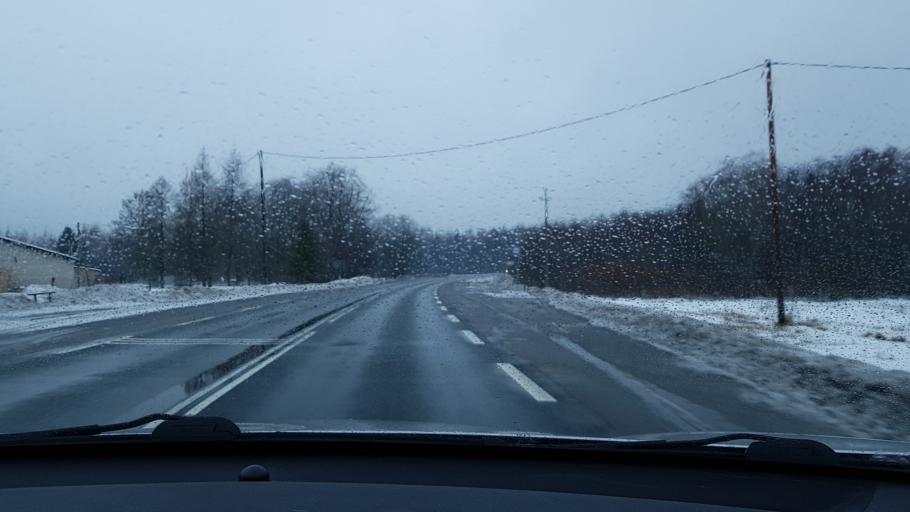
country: EE
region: Jaervamaa
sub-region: Tueri vald
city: Sarevere
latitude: 58.8116
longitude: 25.3513
